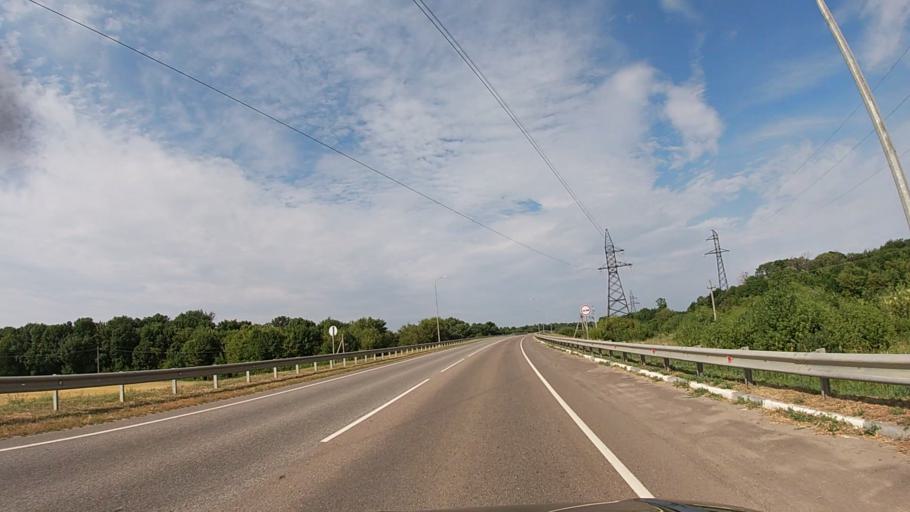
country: RU
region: Belgorod
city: Proletarskiy
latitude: 50.8046
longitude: 35.7402
